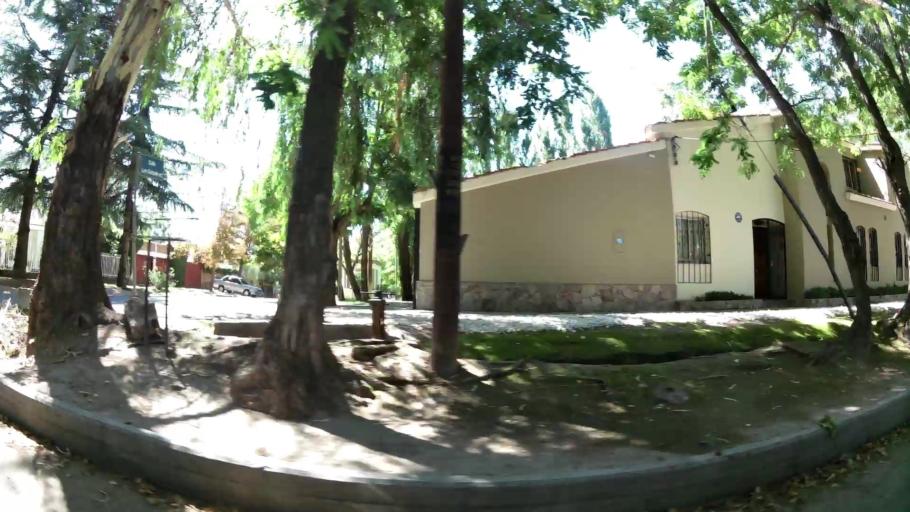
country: AR
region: Mendoza
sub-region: Departamento de Godoy Cruz
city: Godoy Cruz
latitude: -32.9708
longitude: -68.8722
